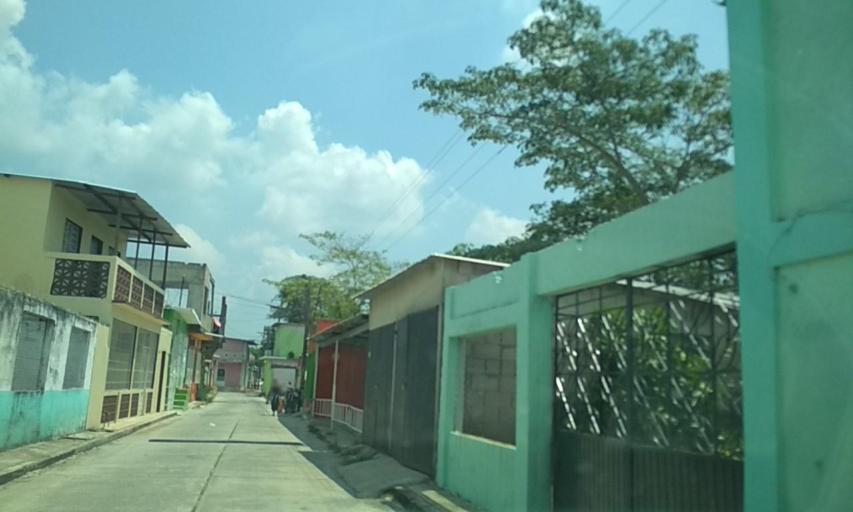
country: MX
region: Veracruz
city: Las Choapas
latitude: 17.9093
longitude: -94.0885
